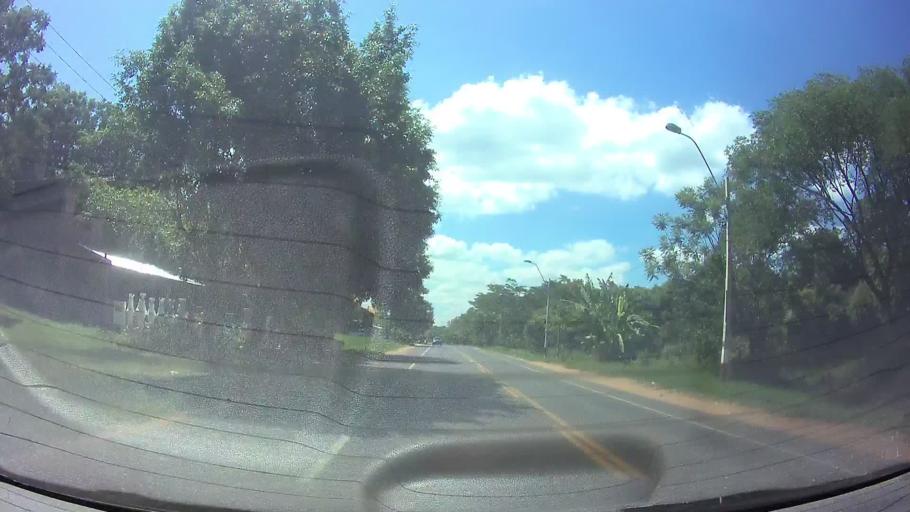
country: PY
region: Central
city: Aregua
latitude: -25.3179
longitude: -57.3721
